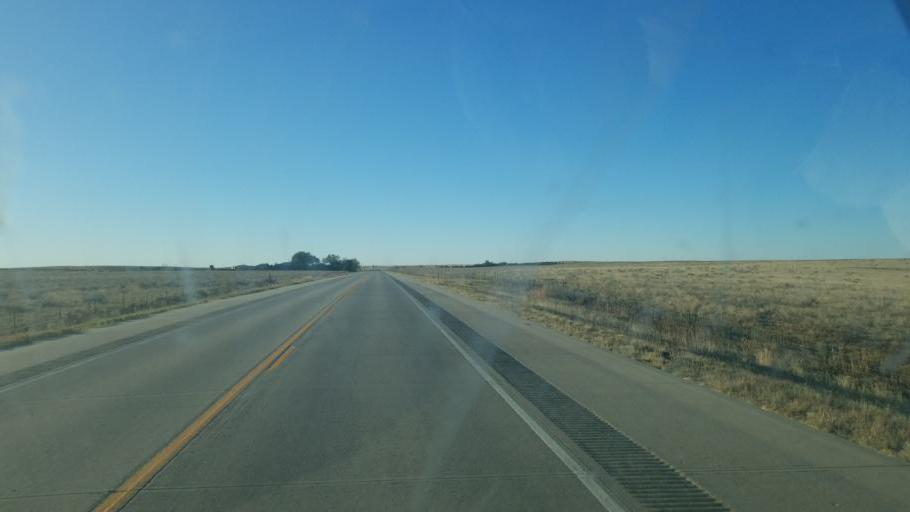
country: US
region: Colorado
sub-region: Kiowa County
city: Eads
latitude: 38.5947
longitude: -102.7860
